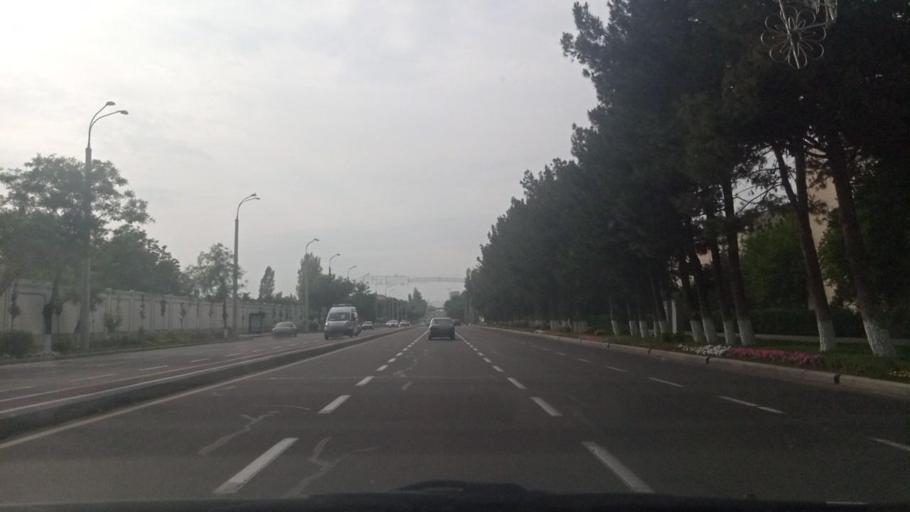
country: UZ
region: Toshkent
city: Salor
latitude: 41.3253
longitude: 69.3610
